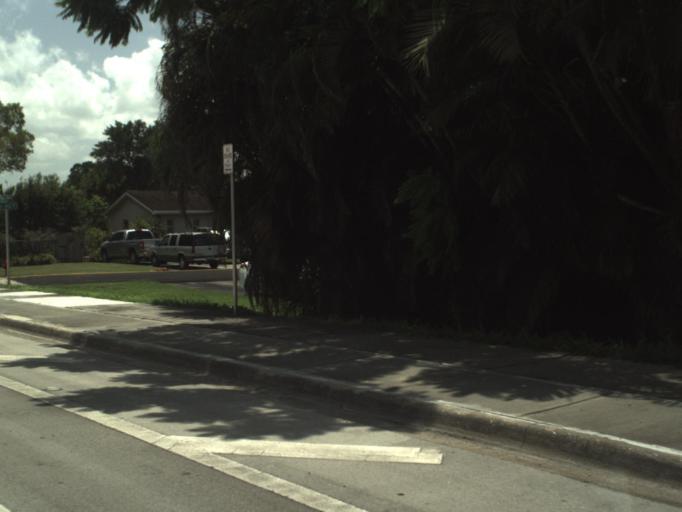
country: US
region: Florida
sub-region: Palm Beach County
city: Belle Glade
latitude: 26.6916
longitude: -80.6679
